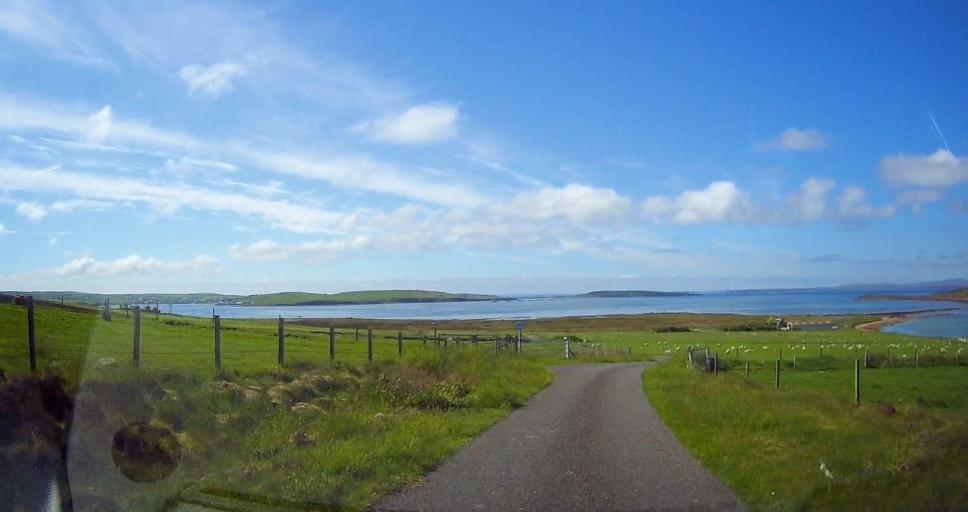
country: GB
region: Scotland
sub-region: Orkney Islands
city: Orkney
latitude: 58.8538
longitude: -2.9516
